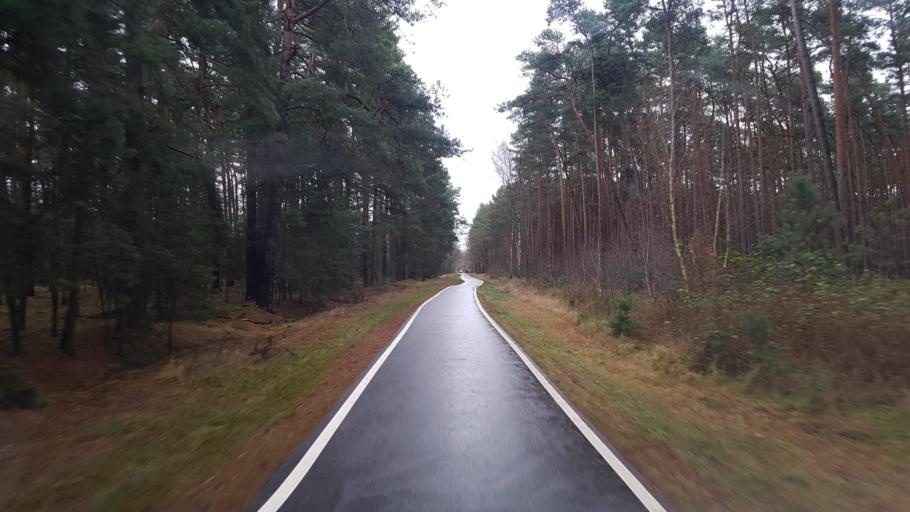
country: DE
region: Brandenburg
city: Tauche
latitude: 52.0918
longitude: 14.1299
